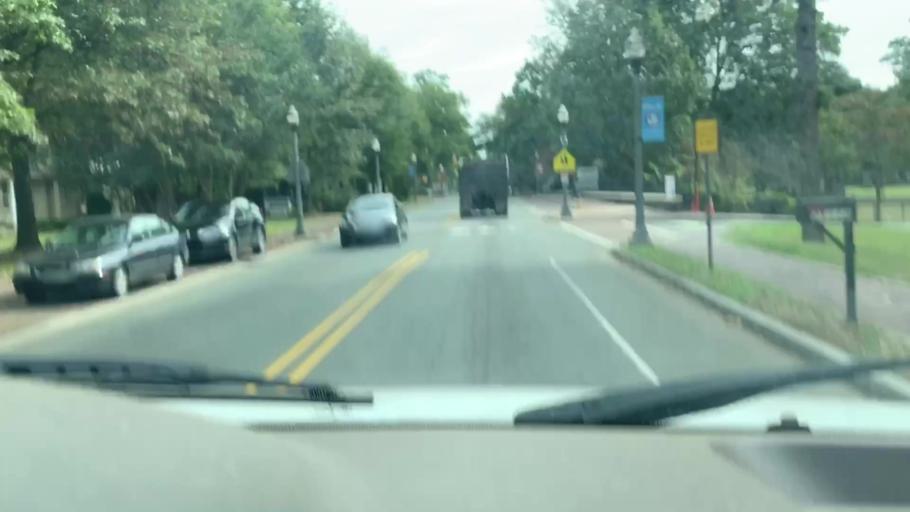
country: US
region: North Carolina
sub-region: Mecklenburg County
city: Cornelius
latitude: 35.4830
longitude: -80.8640
